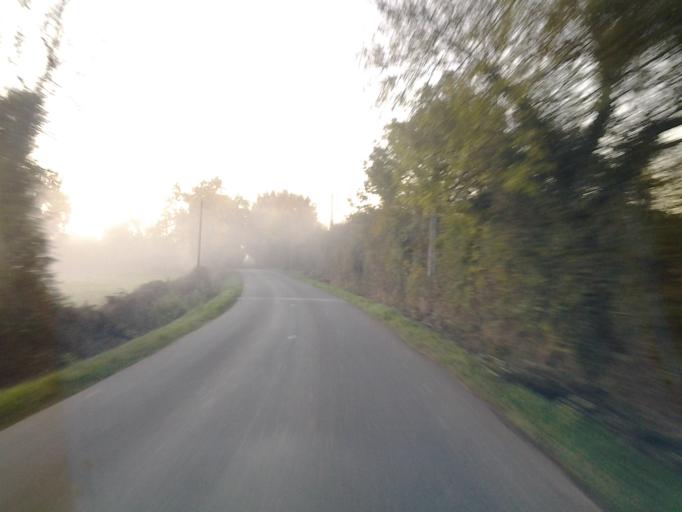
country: FR
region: Pays de la Loire
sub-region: Departement de la Vendee
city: Chateau-Guibert
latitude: 46.6344
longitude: -1.2338
